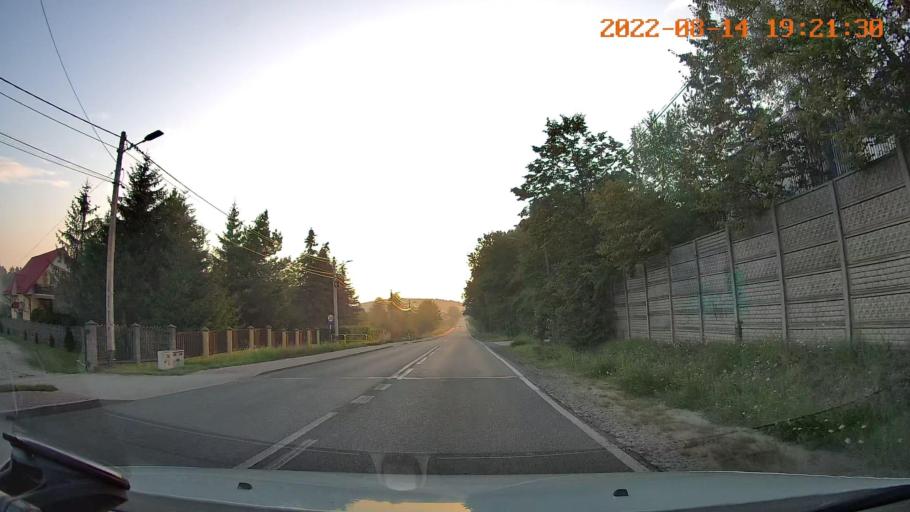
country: PL
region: Swietokrzyskie
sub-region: Powiat kielecki
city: Piekoszow
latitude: 50.8589
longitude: 20.4941
